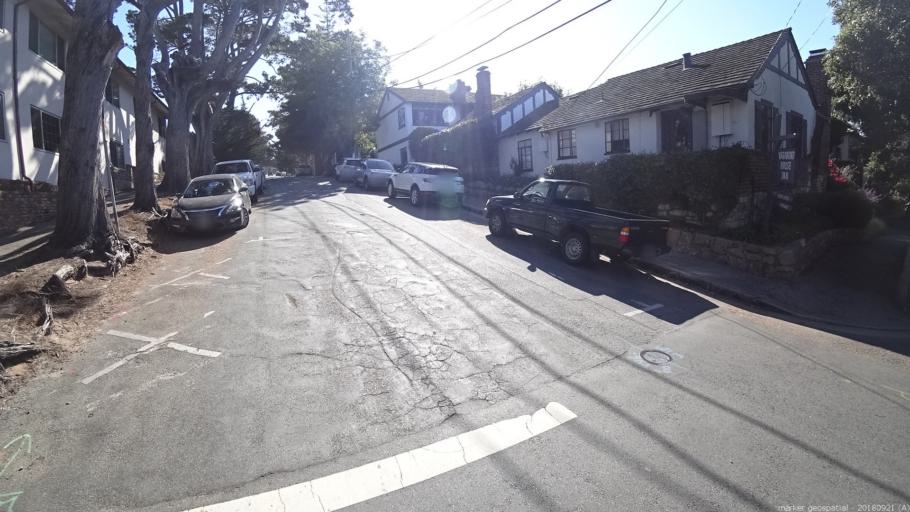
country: US
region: California
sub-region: Monterey County
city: Carmel-by-the-Sea
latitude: 36.5581
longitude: -121.9226
